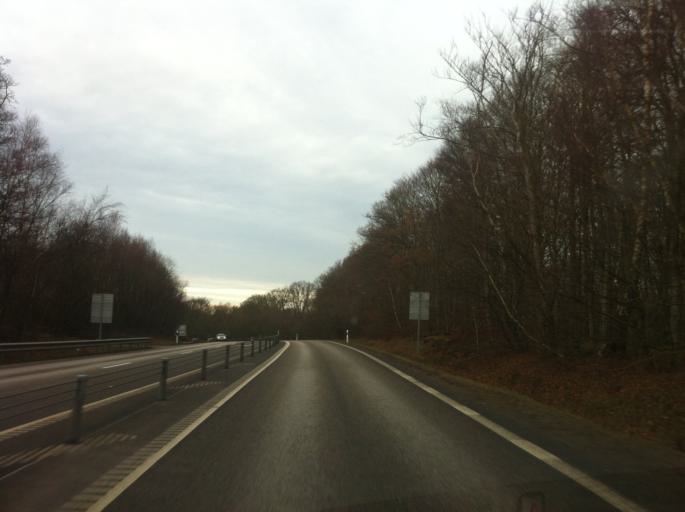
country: DK
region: Capital Region
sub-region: Helsingor Kommune
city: Hellebaek
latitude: 56.1238
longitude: 12.6175
